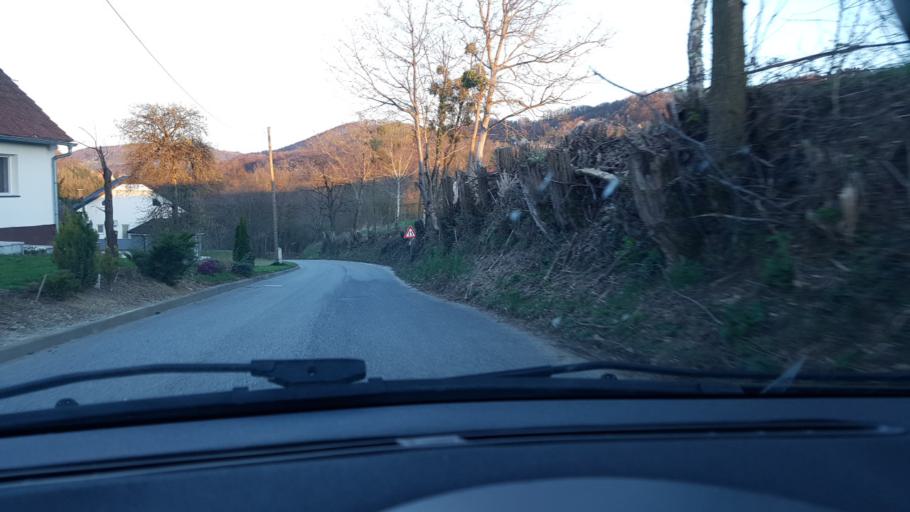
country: SI
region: Rogatec
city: Rogatec
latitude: 46.1945
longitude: 15.6846
